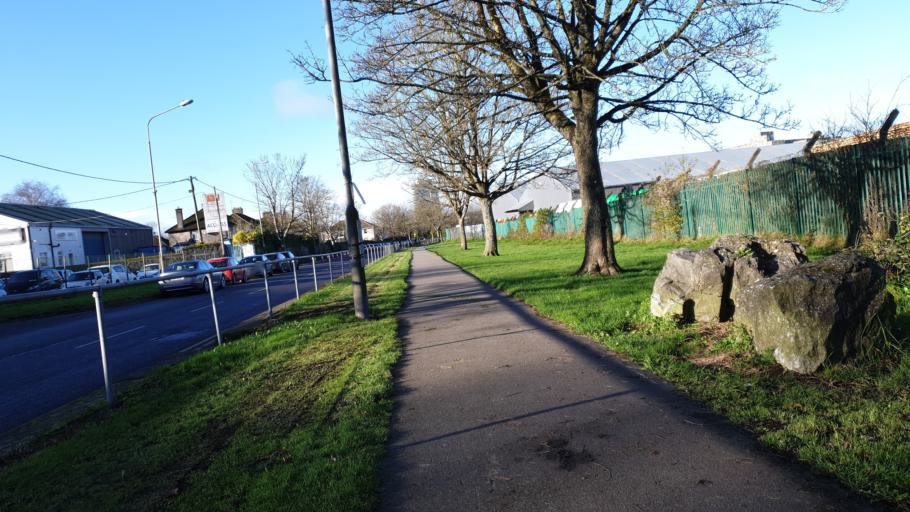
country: IE
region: Munster
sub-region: County Cork
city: Cork
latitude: 51.8955
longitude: -8.4514
